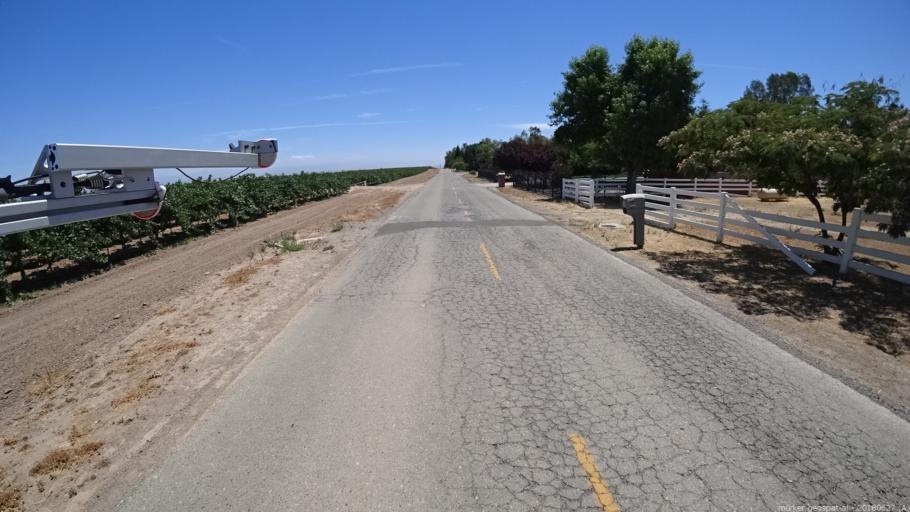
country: US
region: California
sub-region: Madera County
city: Bonadelle Ranchos-Madera Ranchos
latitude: 36.9375
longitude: -119.8810
